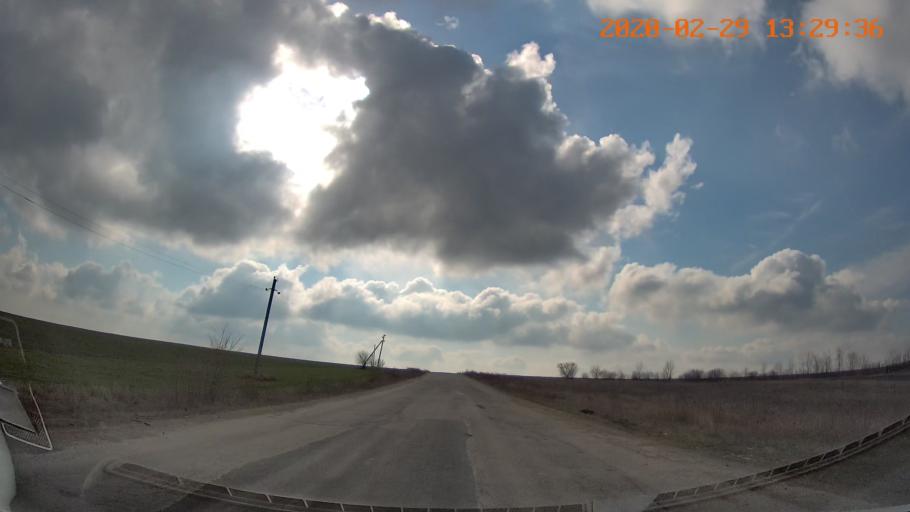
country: MD
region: Telenesti
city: Camenca
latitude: 47.8952
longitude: 28.6353
